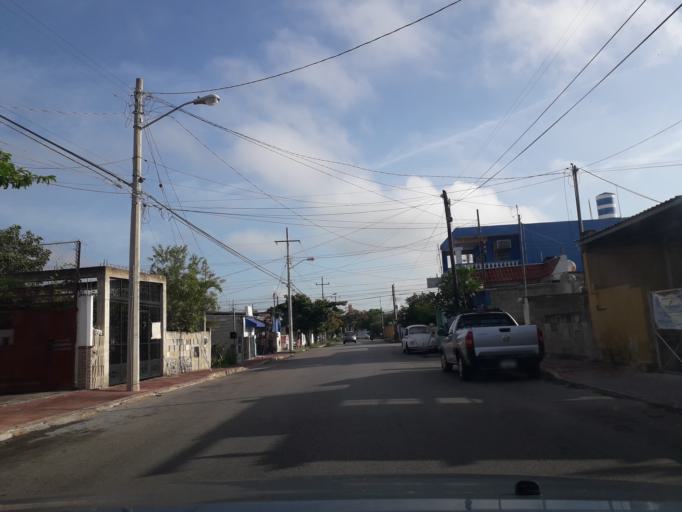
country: MX
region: Yucatan
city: Merida
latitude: 20.9797
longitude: -89.6542
